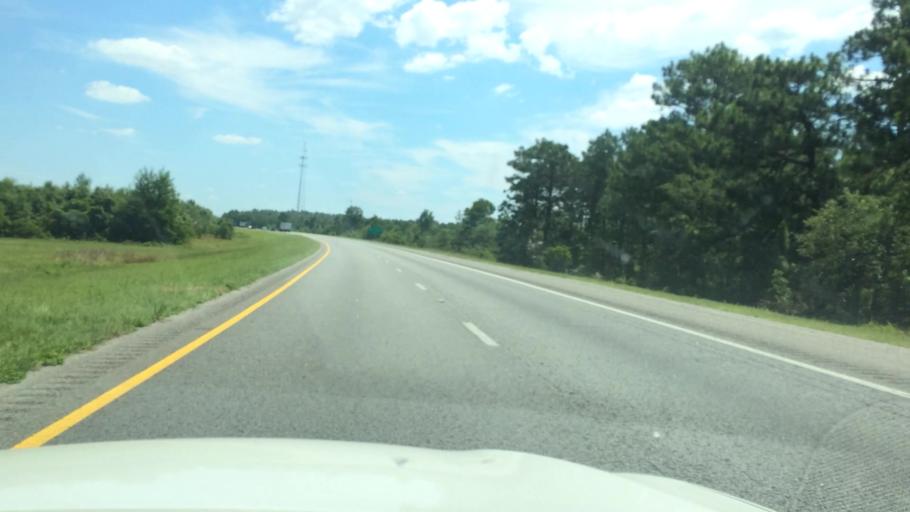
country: US
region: South Carolina
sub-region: Aiken County
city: Aiken
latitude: 33.7089
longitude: -81.5859
